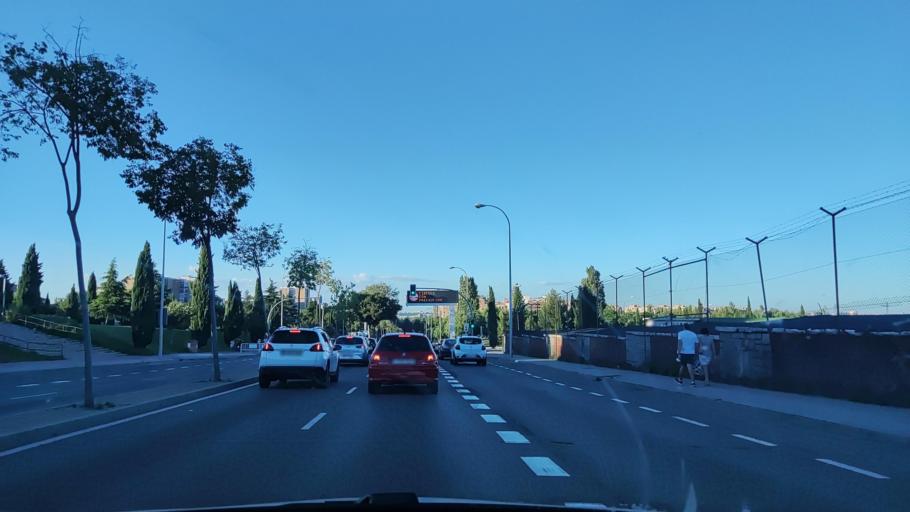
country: ES
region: Madrid
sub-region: Provincia de Madrid
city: Latina
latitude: 40.3703
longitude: -3.7379
